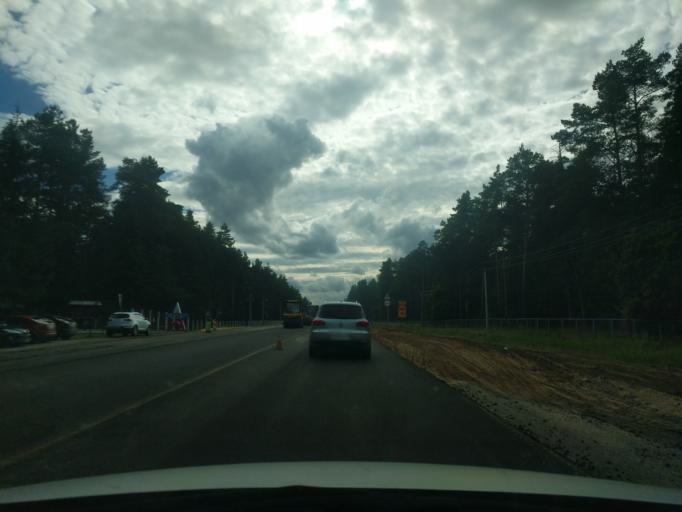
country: RU
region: Jaroslavl
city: Levashevo
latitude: 57.6777
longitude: 40.5910
